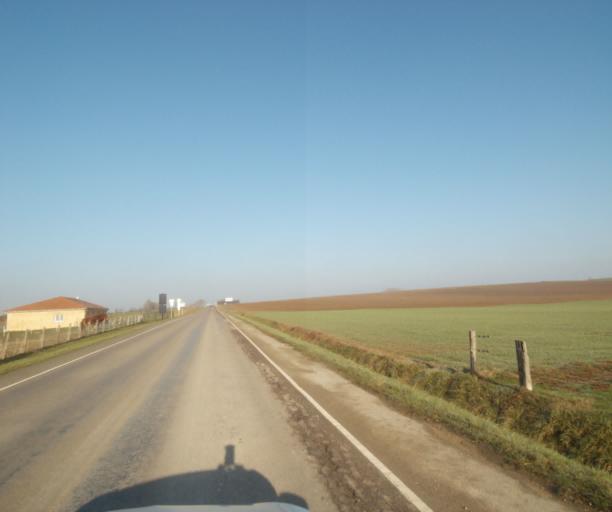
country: FR
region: Champagne-Ardenne
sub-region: Departement de la Haute-Marne
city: Montier-en-Der
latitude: 48.4884
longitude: 4.7588
